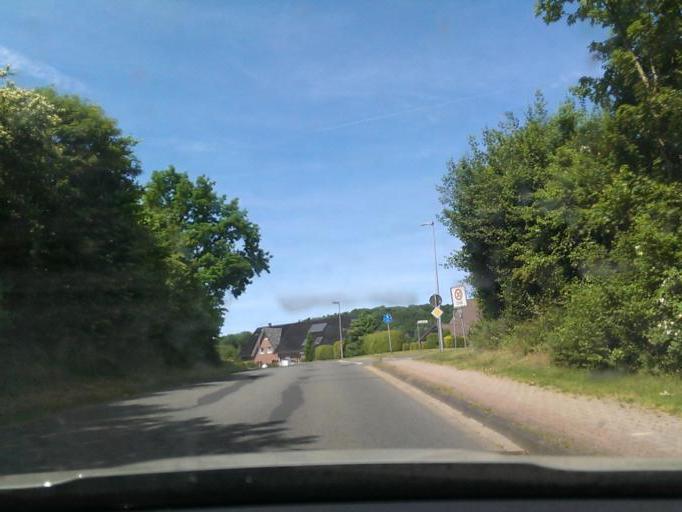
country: DE
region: Lower Saxony
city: Alfeld
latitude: 51.9839
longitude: 9.8039
